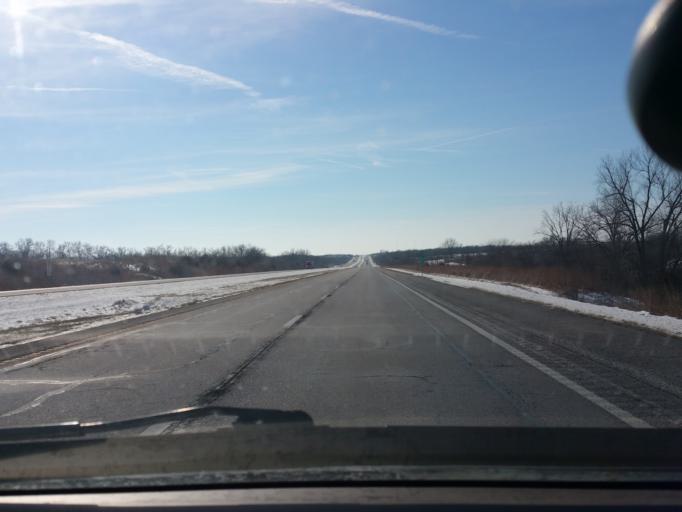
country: US
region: Missouri
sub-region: Harrison County
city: Bethany
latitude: 40.4176
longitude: -93.9909
